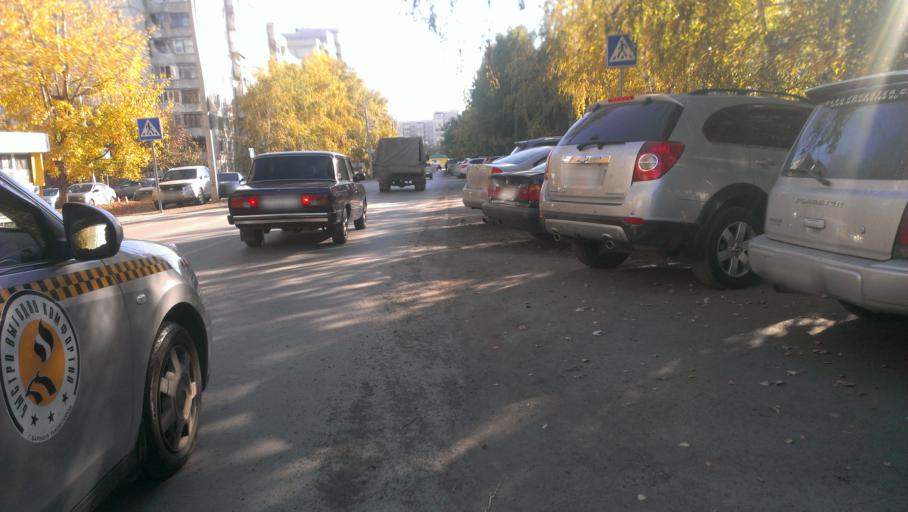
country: RU
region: Altai Krai
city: Novosilikatnyy
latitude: 53.3474
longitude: 83.6757
